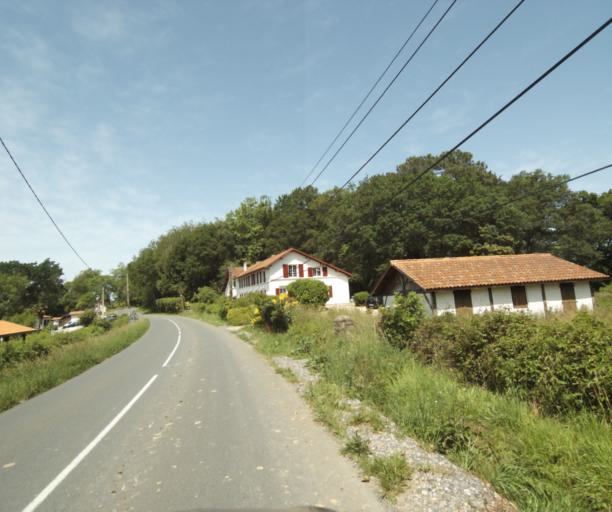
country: FR
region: Aquitaine
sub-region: Departement des Pyrenees-Atlantiques
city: Mouguerre
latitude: 43.4545
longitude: -1.4265
